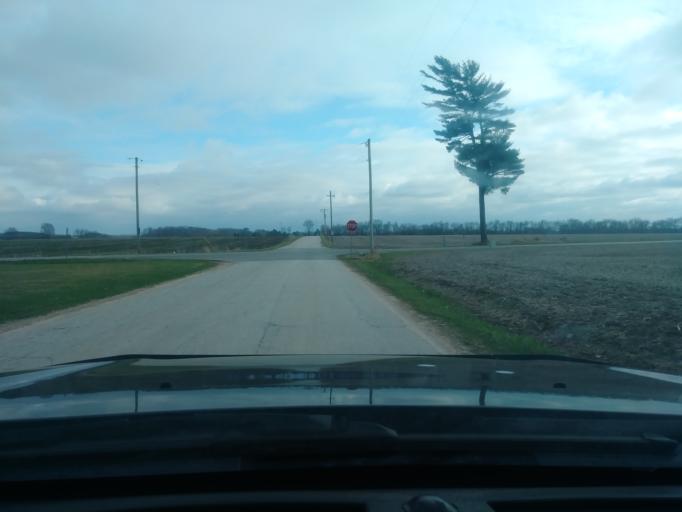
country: US
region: Indiana
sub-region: LaPorte County
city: LaPorte
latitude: 41.5674
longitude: -86.7983
